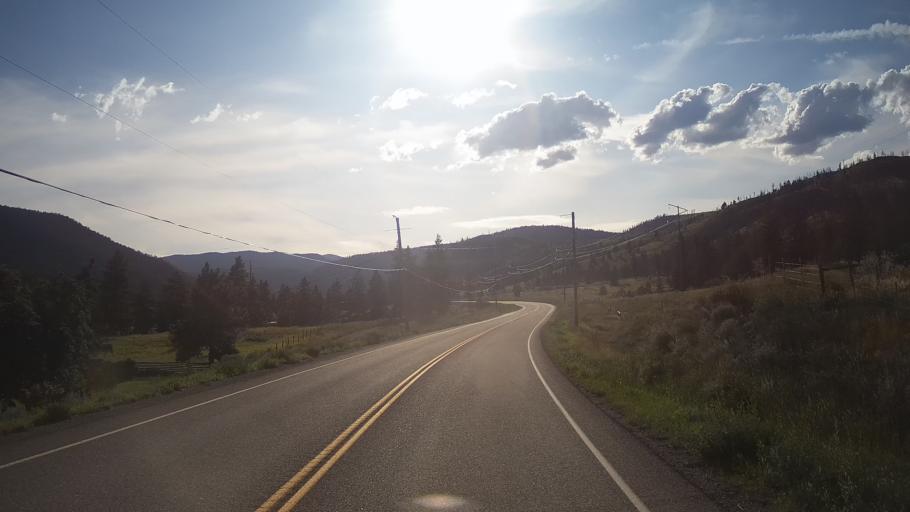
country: CA
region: British Columbia
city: Cache Creek
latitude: 50.8868
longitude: -121.4594
